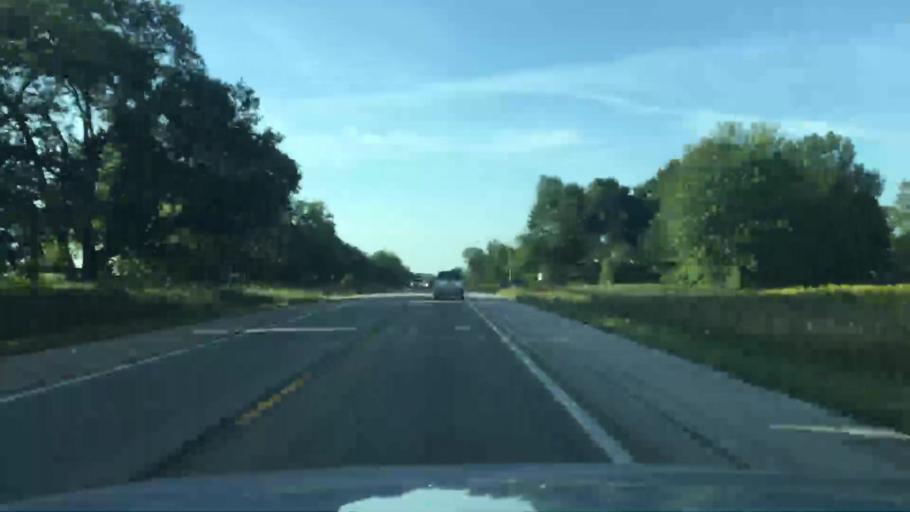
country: US
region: Michigan
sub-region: Jackson County
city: Vandercook Lake
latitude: 42.1042
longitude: -84.3639
